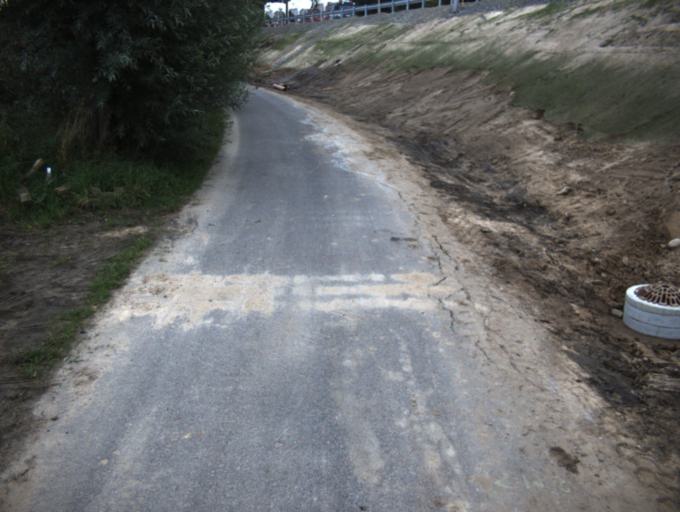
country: SE
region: Skane
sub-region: Helsingborg
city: Odakra
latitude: 56.0770
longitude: 12.7364
